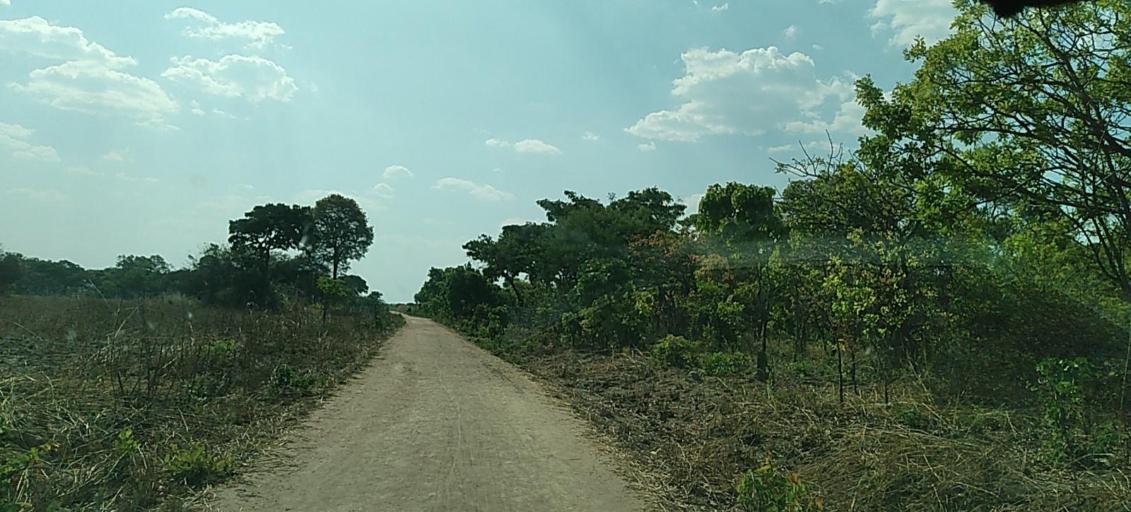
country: ZM
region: North-Western
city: Kalengwa
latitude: -13.0991
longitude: 24.9835
